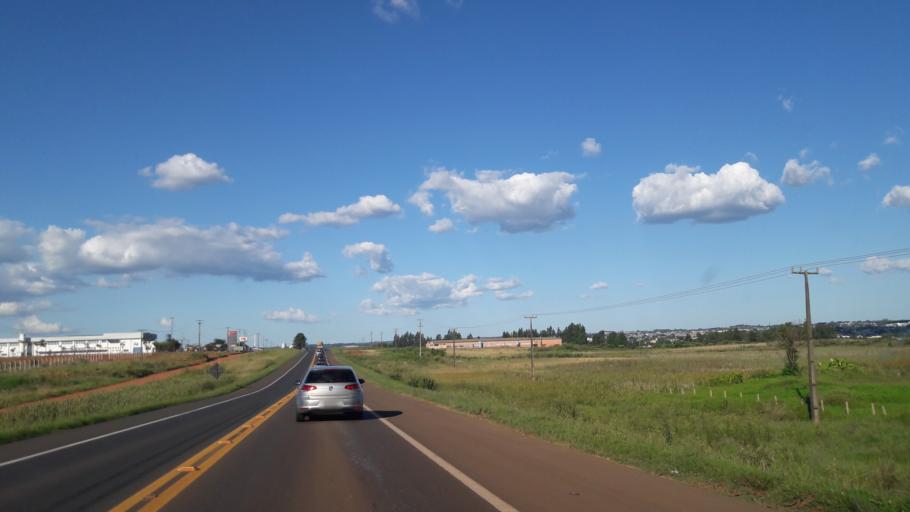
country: BR
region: Parana
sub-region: Guarapuava
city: Guarapuava
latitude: -25.3845
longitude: -51.5132
